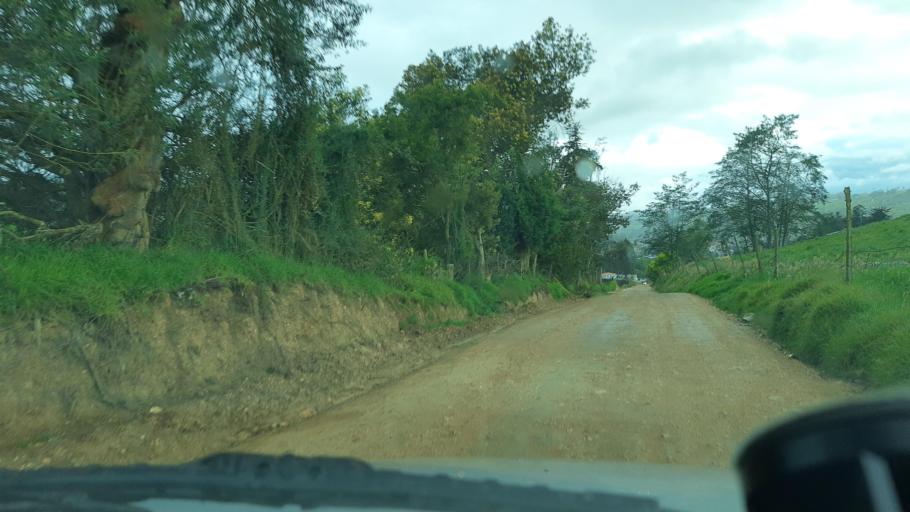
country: CO
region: Cundinamarca
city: Villapinzon
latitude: 5.2282
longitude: -73.5843
